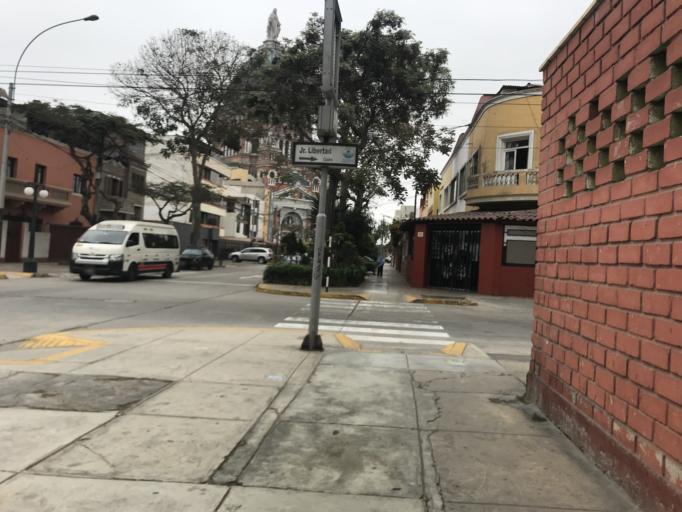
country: PE
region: Lima
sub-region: Lima
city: San Isidro
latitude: -12.0871
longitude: -77.0675
